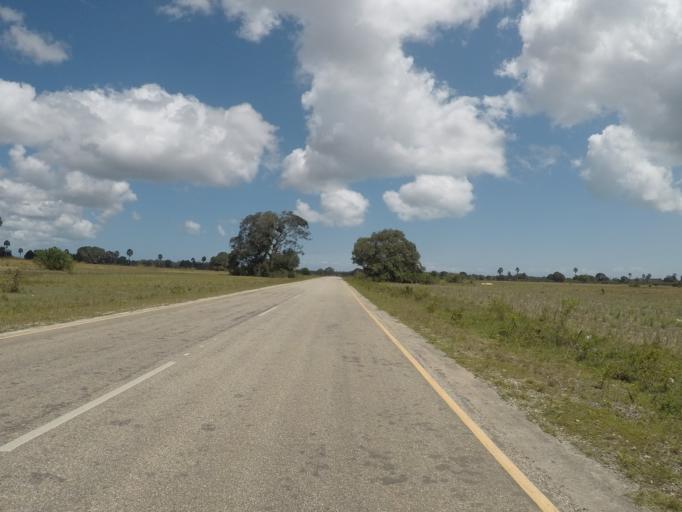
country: TZ
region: Zanzibar Central/South
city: Koani
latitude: -6.2166
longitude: 39.3642
